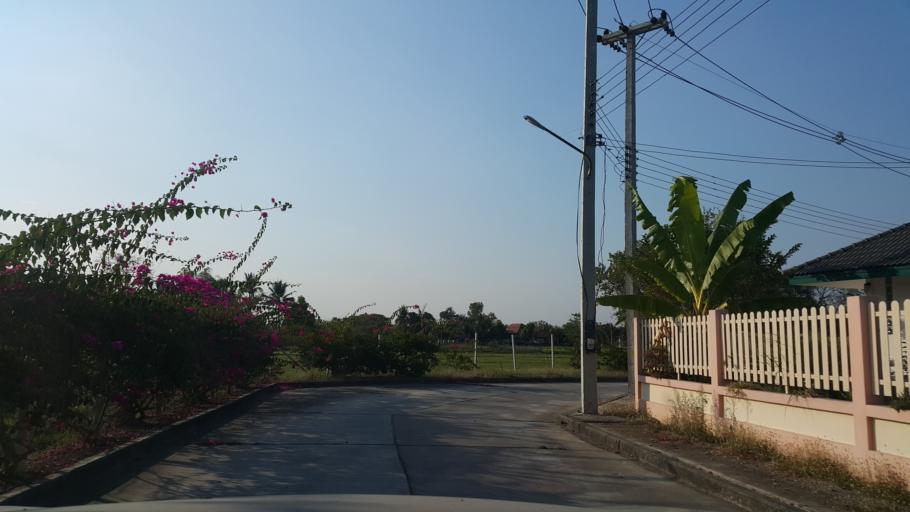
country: TH
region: Chiang Mai
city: San Sai
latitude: 18.8379
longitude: 99.0948
